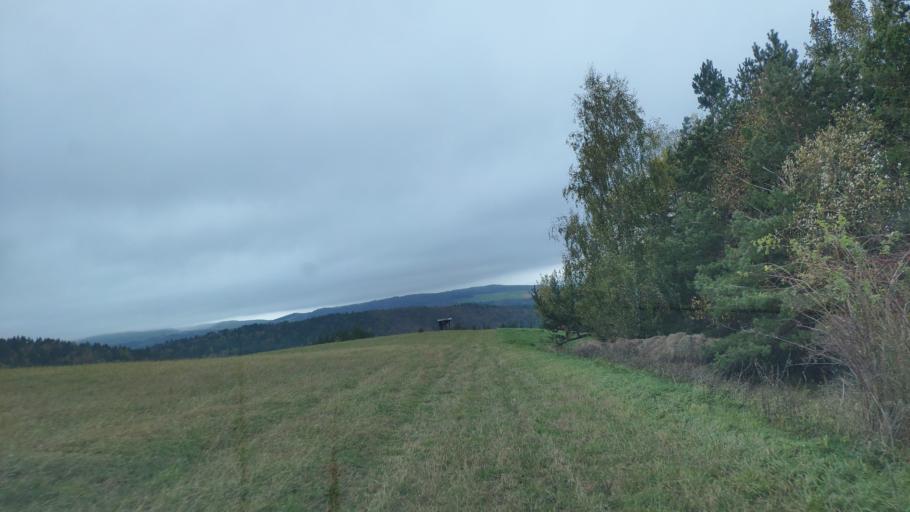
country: SK
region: Presovsky
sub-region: Okres Presov
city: Presov
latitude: 48.9364
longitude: 21.1182
